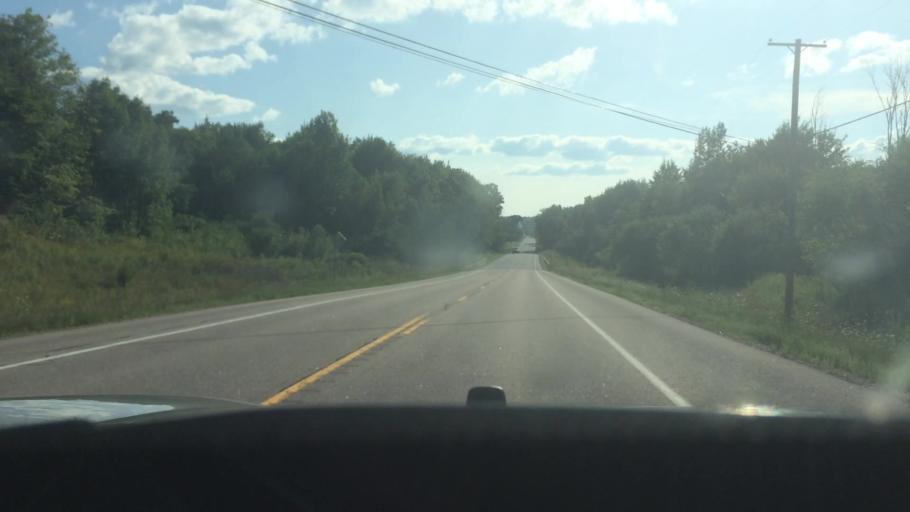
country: US
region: New York
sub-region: Franklin County
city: Malone
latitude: 44.7477
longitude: -74.5657
